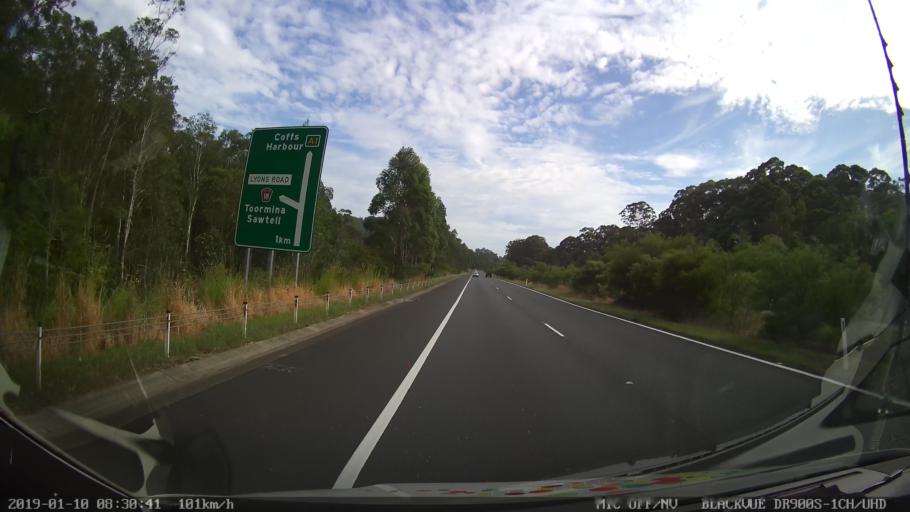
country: AU
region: New South Wales
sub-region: Coffs Harbour
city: Bonville
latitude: -30.3663
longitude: 153.0549
